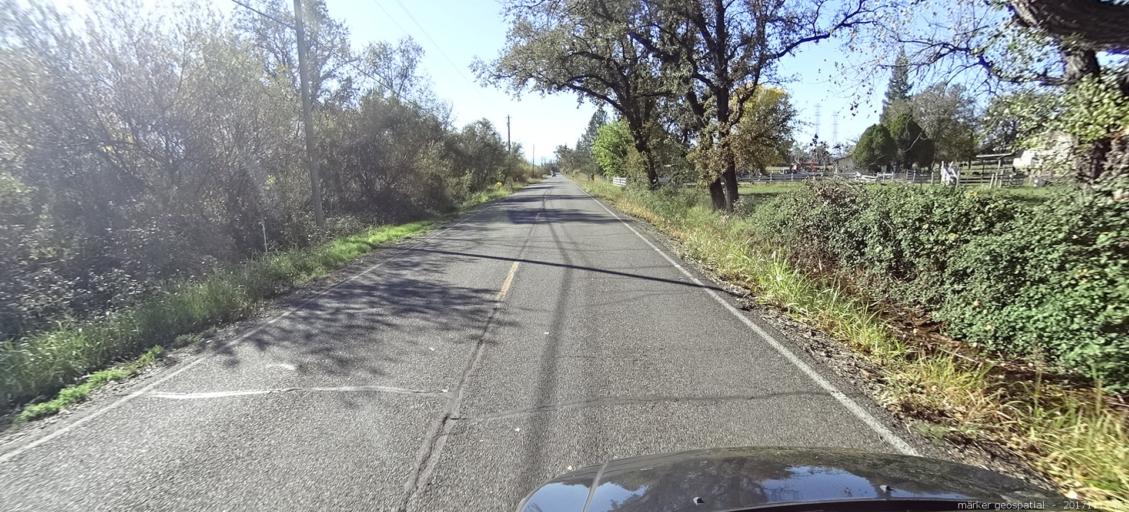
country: US
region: California
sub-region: Shasta County
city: Cottonwood
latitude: 40.3918
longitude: -122.2633
